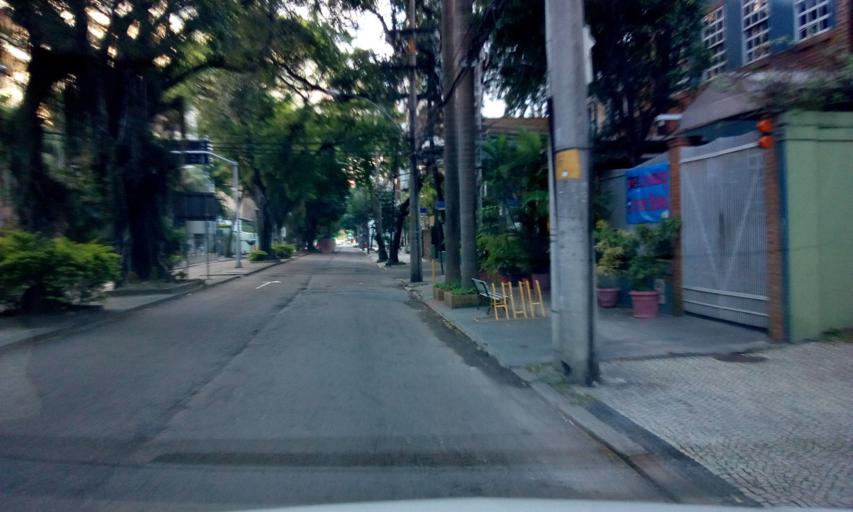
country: BR
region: Rio de Janeiro
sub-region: Rio De Janeiro
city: Rio de Janeiro
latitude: -22.9645
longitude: -43.2027
